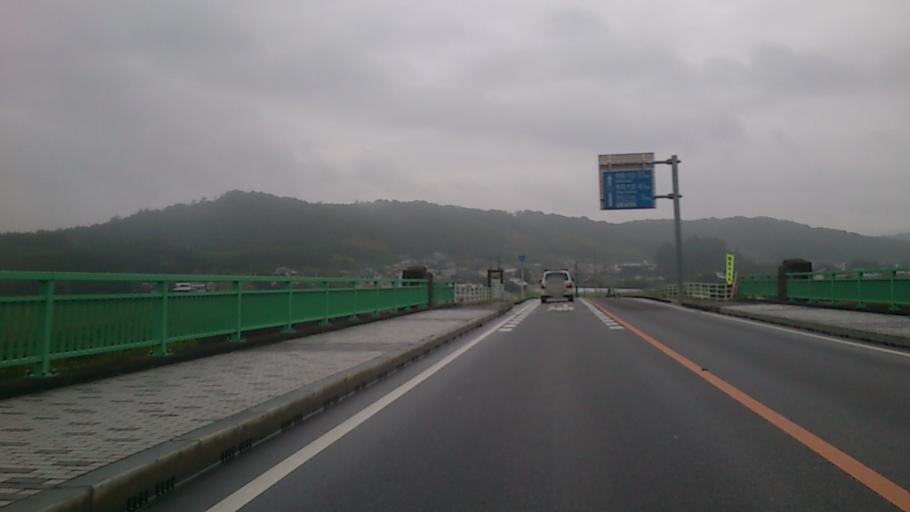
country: JP
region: Tochigi
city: Karasuyama
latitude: 36.7498
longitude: 140.1408
